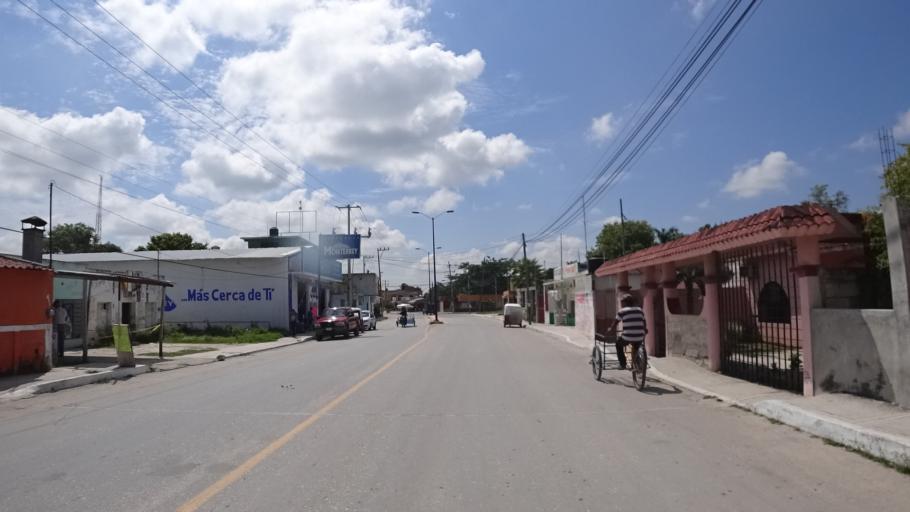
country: MX
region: Campeche
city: Sabancuy
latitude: 18.9706
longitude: -91.1786
